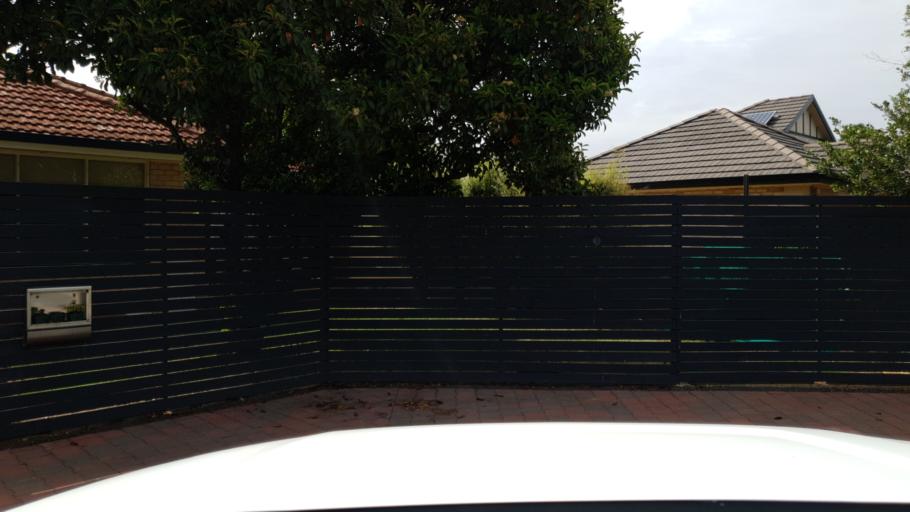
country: AU
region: South Australia
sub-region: Mitcham
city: Clarence Gardens
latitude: -34.9713
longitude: 138.5749
